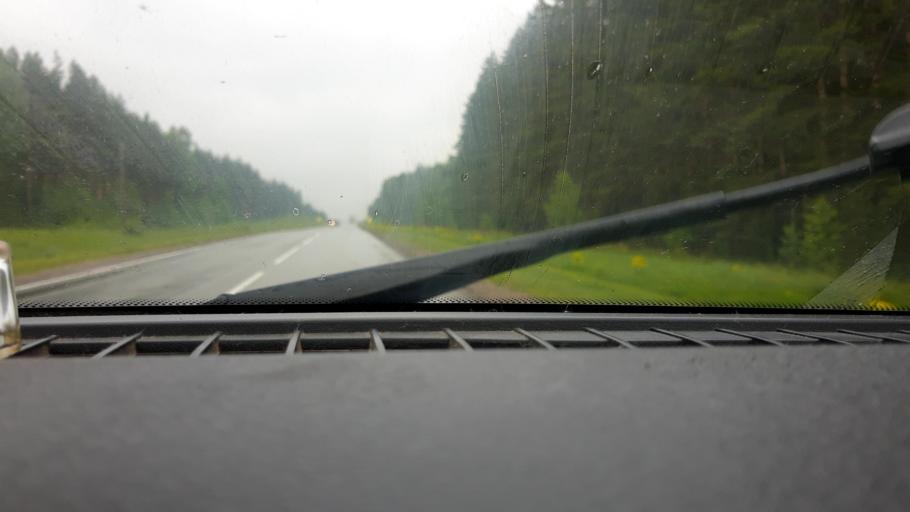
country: RU
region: Bashkortostan
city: Belebey
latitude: 54.2134
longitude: 54.0763
